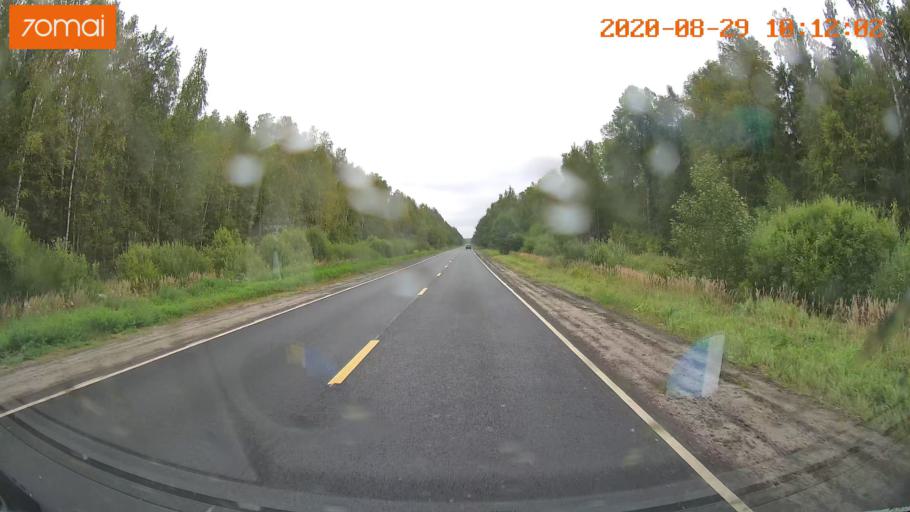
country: RU
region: Ivanovo
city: Kuznechikha
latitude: 57.3736
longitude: 42.6993
